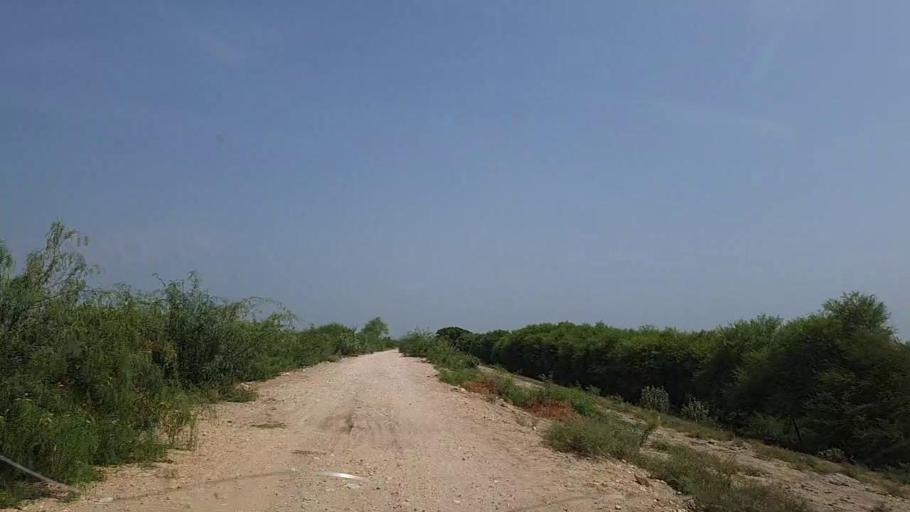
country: PK
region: Sindh
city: Ghotki
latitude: 28.0994
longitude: 69.4020
